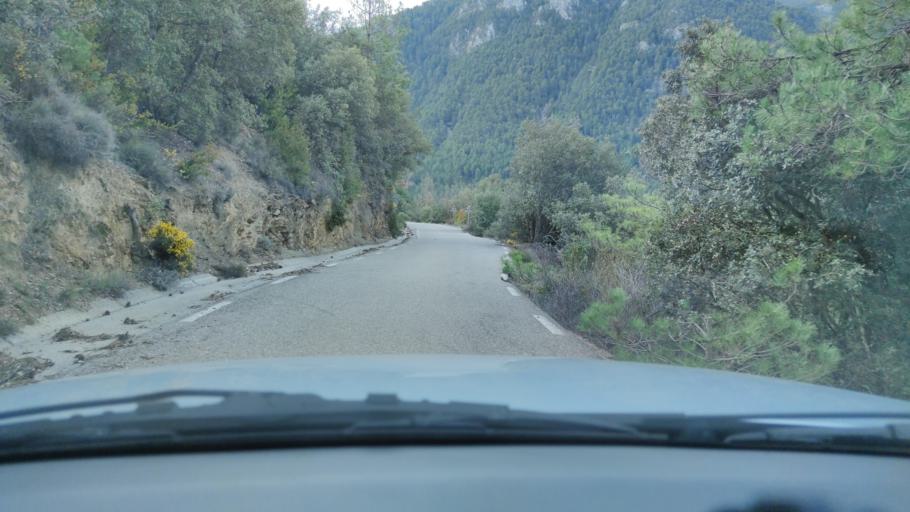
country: ES
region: Catalonia
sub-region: Provincia de Lleida
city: la Seu d'Urgell
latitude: 42.2424
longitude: 1.4314
